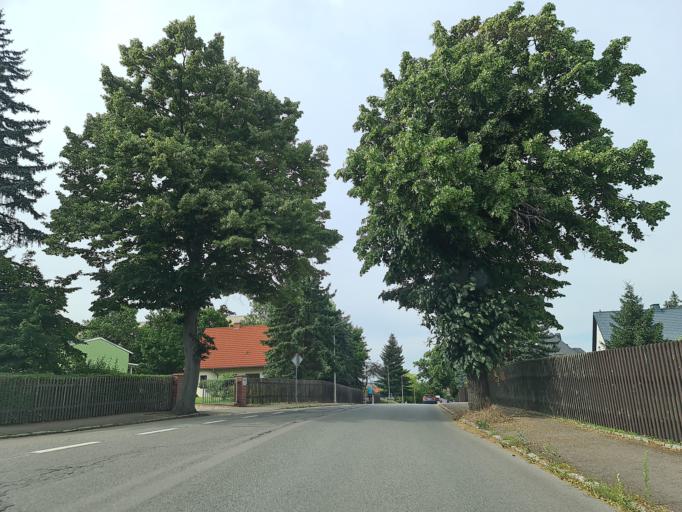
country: DE
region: Saxony
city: Lichtentanne
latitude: 50.6879
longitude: 12.4684
